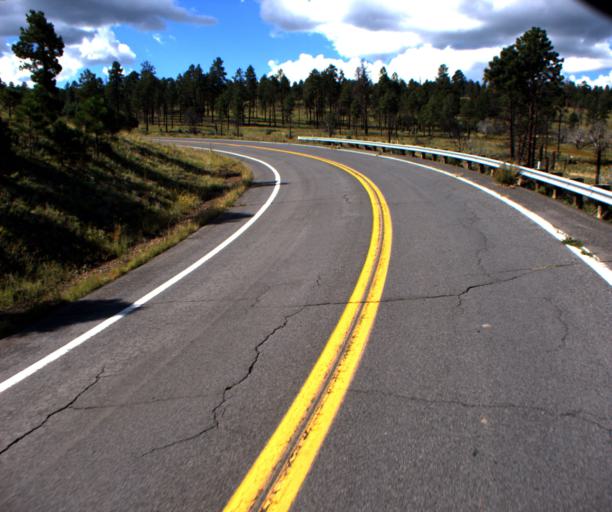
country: US
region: Arizona
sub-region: Apache County
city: Eagar
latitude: 34.0731
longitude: -109.3490
